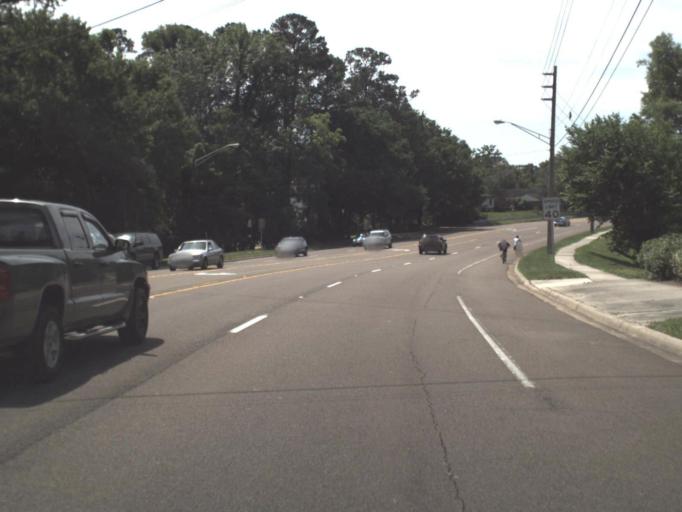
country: US
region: Florida
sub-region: Duval County
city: Jacksonville
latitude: 30.2974
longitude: -81.6480
